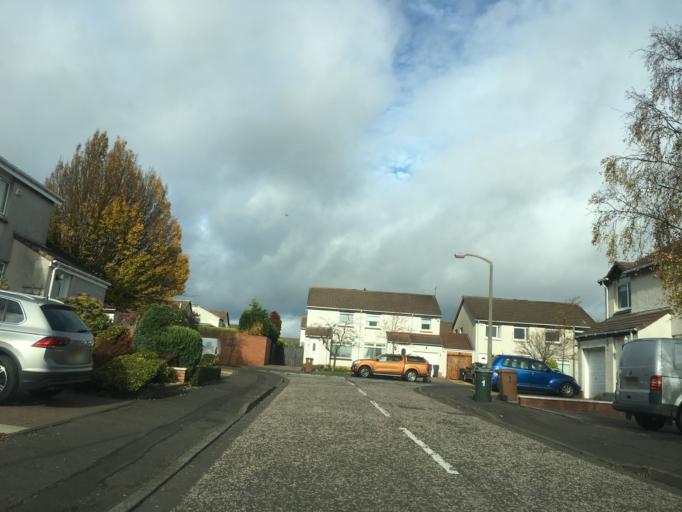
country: GB
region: Scotland
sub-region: Midlothian
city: Loanhead
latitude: 55.9051
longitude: -3.1726
